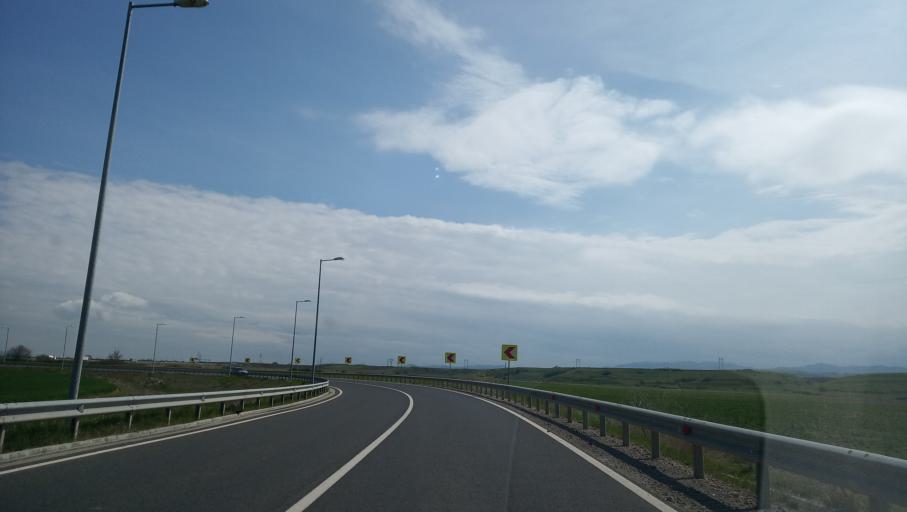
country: RO
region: Hunedoara
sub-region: Comuna Romos
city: Romos
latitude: 45.8878
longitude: 23.2619
